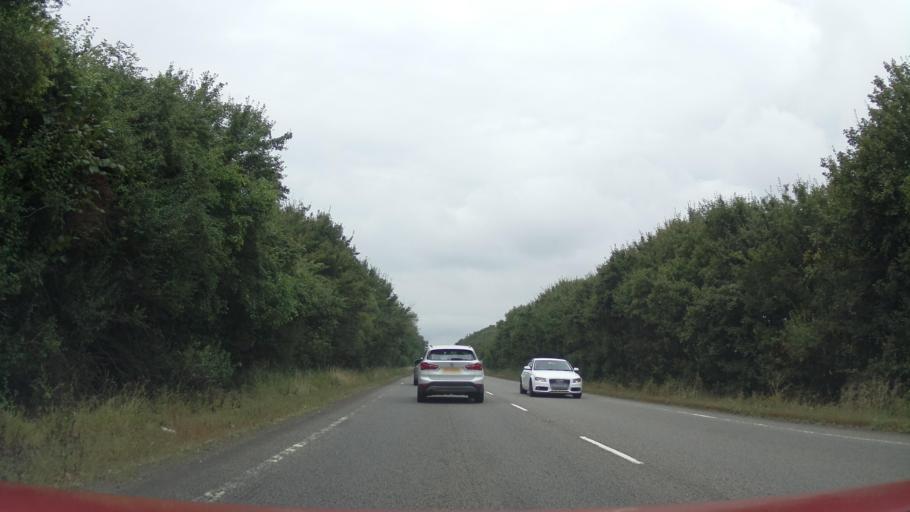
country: GB
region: England
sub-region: Nottinghamshire
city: South Collingham
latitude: 53.0910
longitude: -0.7648
